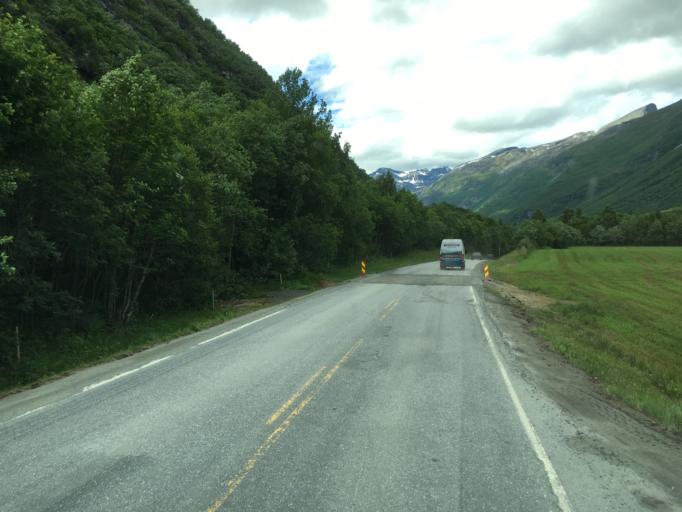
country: NO
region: More og Romsdal
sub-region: Sunndal
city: Sunndalsora
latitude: 62.5980
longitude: 8.9443
